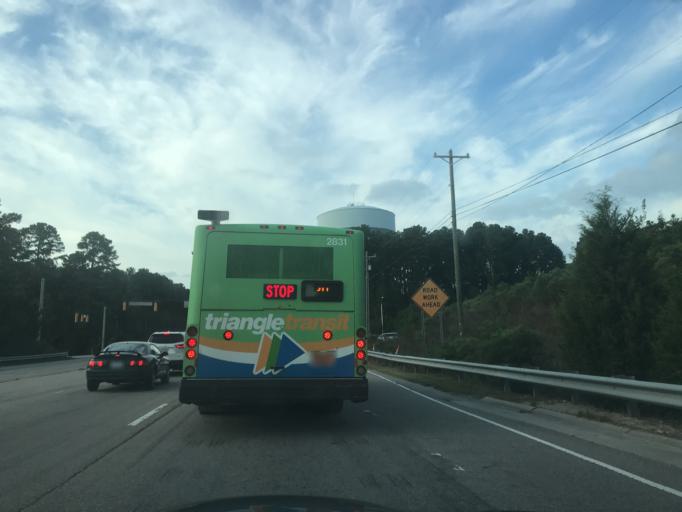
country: US
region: North Carolina
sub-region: Wake County
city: Green Level
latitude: 35.8128
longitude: -78.8724
